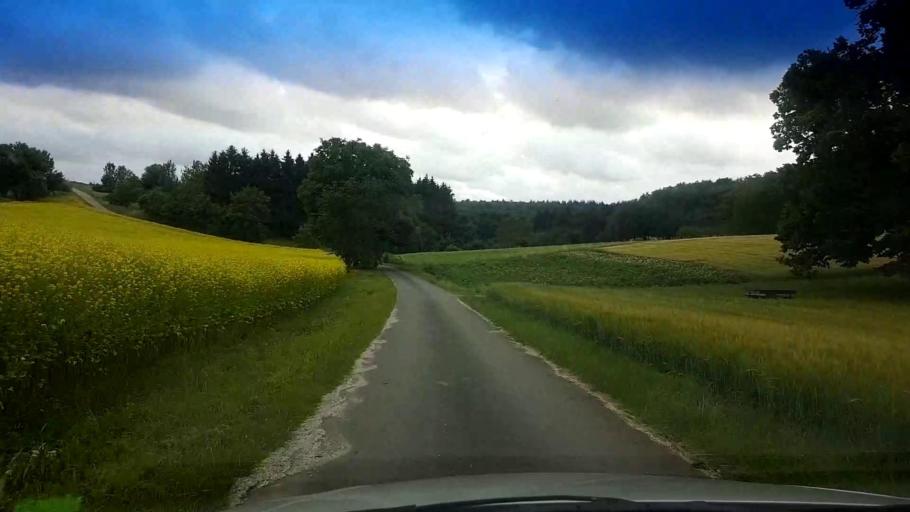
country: DE
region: Bavaria
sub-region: Upper Franconia
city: Poxdorf
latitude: 49.8950
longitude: 11.0803
